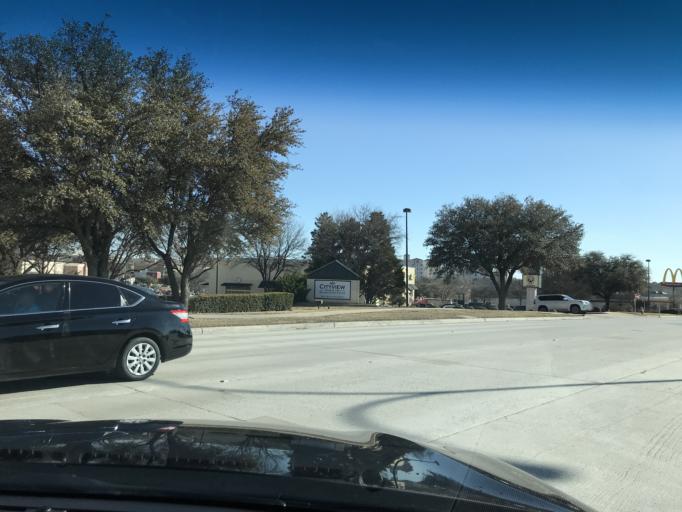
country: US
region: Texas
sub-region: Tarrant County
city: Benbrook
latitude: 32.6640
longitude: -97.4213
